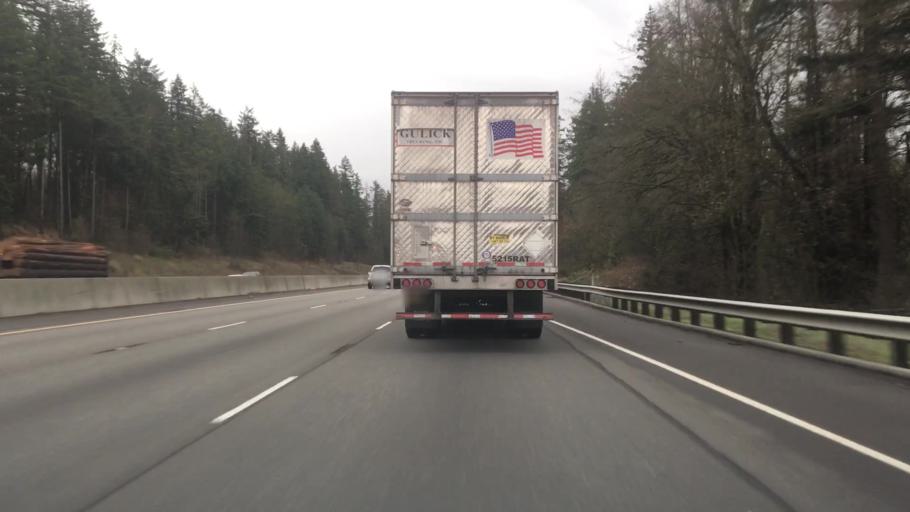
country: US
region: Washington
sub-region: Thurston County
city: Grand Mound
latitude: 46.8635
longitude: -122.9717
